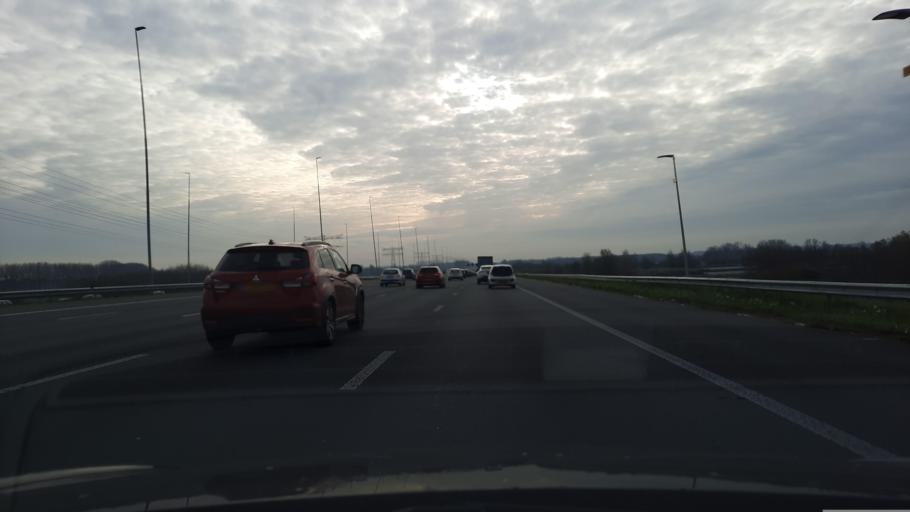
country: NL
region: Utrecht
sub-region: Stichtse Vecht
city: Breukelen
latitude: 52.1594
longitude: 4.9896
